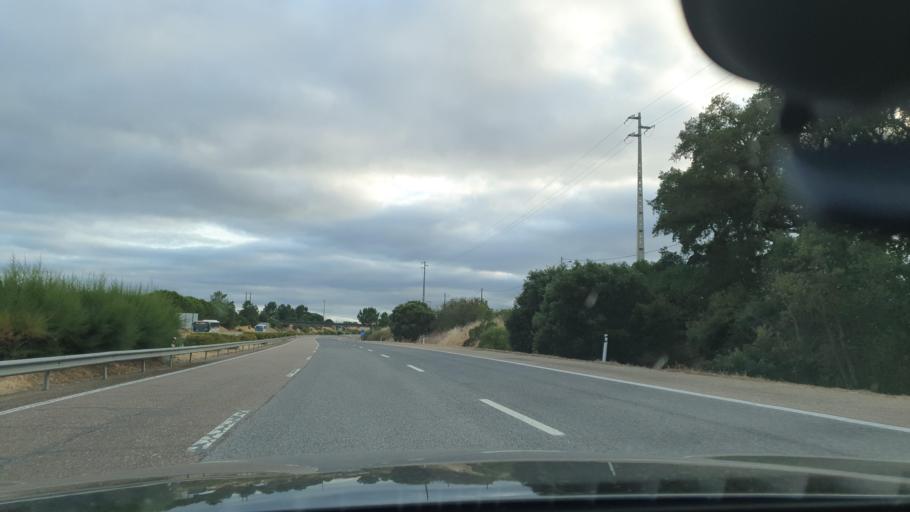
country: PT
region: Setubal
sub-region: Montijo
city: Montijo
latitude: 38.7198
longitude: -8.9271
